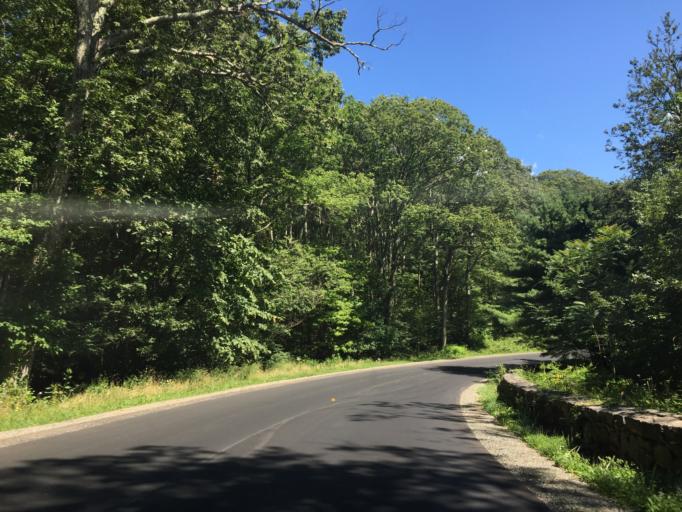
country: US
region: Virginia
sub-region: Page County
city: Luray
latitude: 38.6685
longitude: -78.3307
